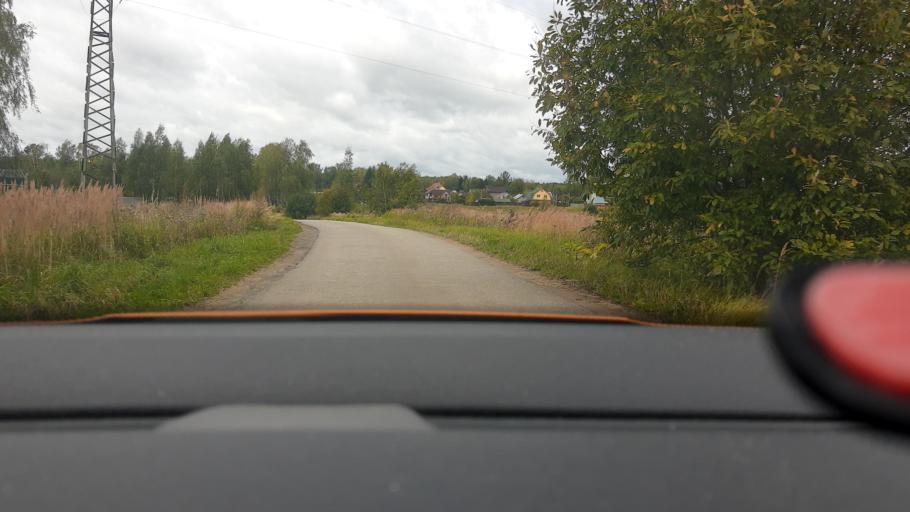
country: RU
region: Moskovskaya
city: Krasnoarmeysk
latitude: 56.0883
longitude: 38.0320
